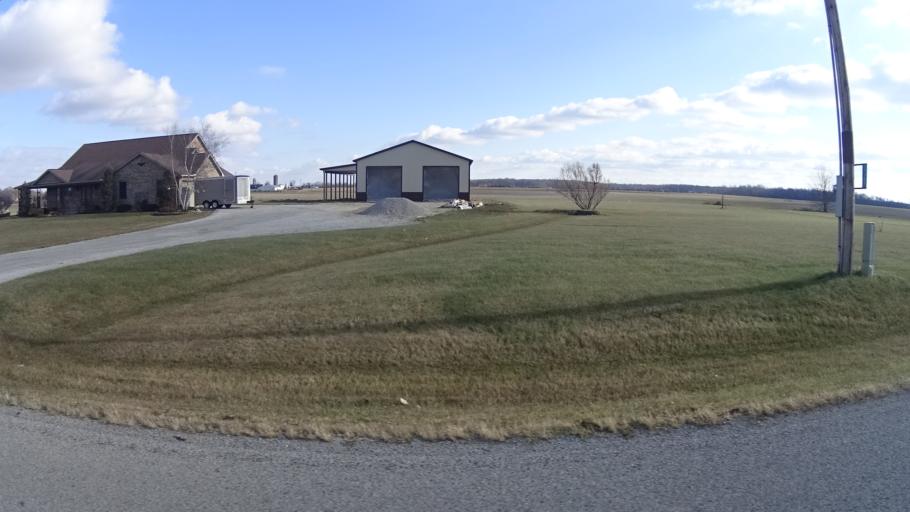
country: US
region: Ohio
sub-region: Lorain County
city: Camden
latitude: 41.2343
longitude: -82.2895
